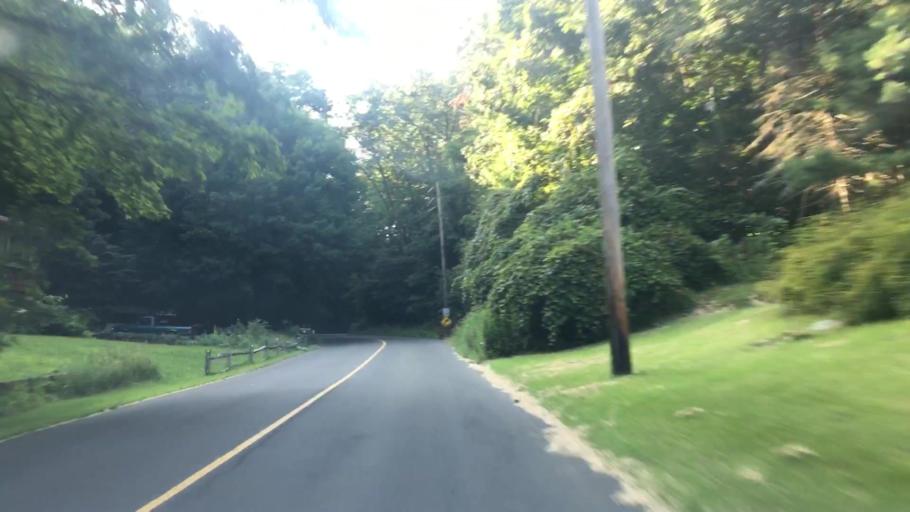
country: US
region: Connecticut
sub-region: Middlesex County
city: Chester Center
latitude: 41.3914
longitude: -72.4469
